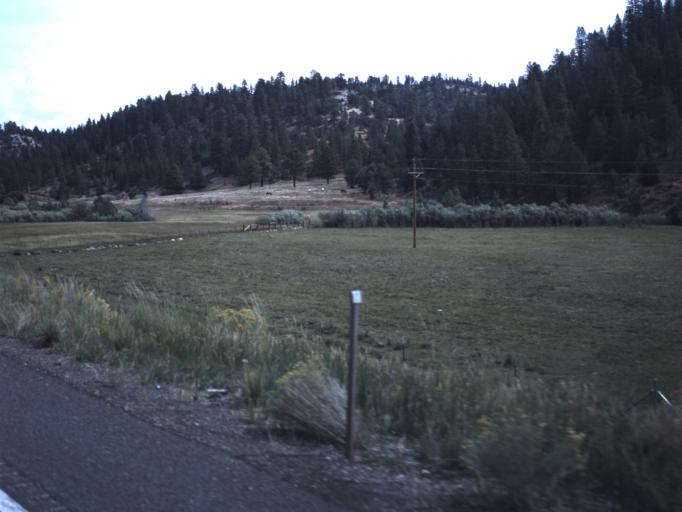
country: US
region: Utah
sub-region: Kane County
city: Kanab
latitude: 37.4085
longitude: -112.5513
